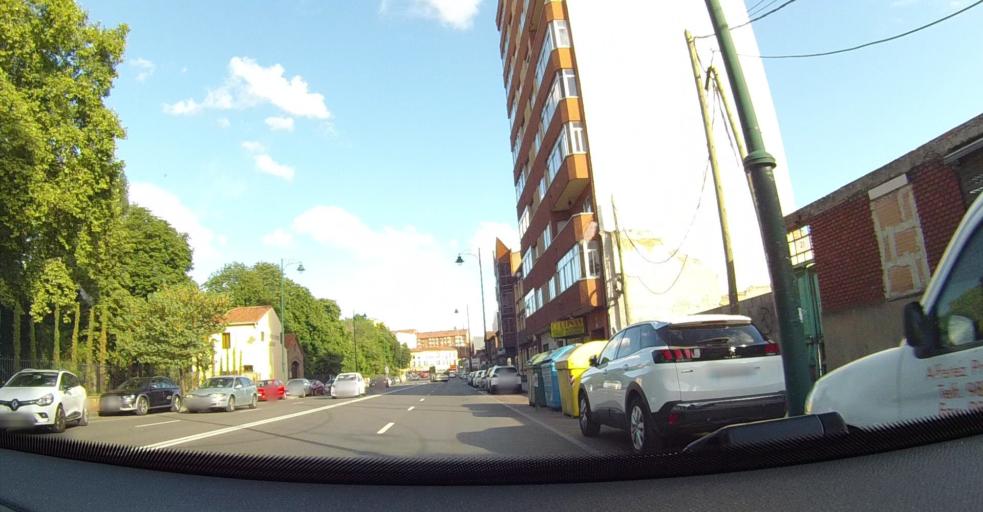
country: ES
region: Castille and Leon
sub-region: Provincia de Leon
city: Leon
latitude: 42.6018
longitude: -5.5878
